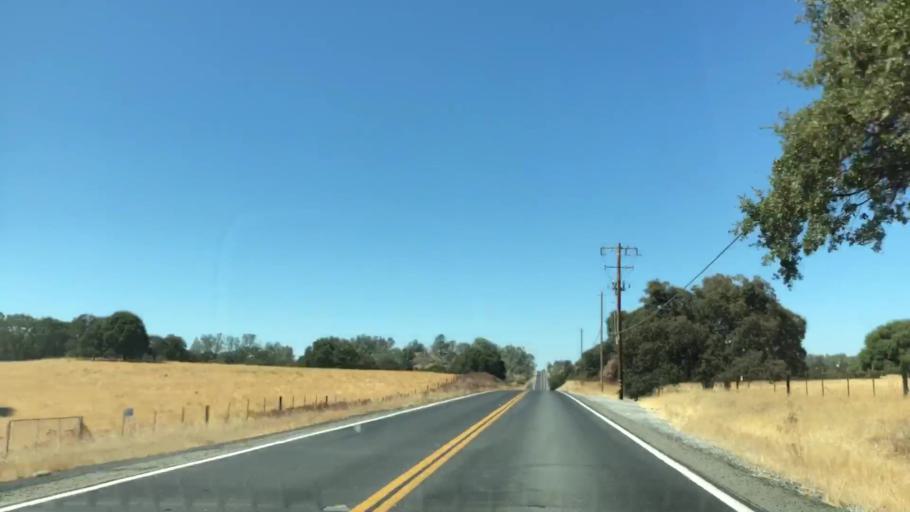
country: US
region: California
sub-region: Tuolumne County
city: Jamestown
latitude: 37.8884
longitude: -120.5203
